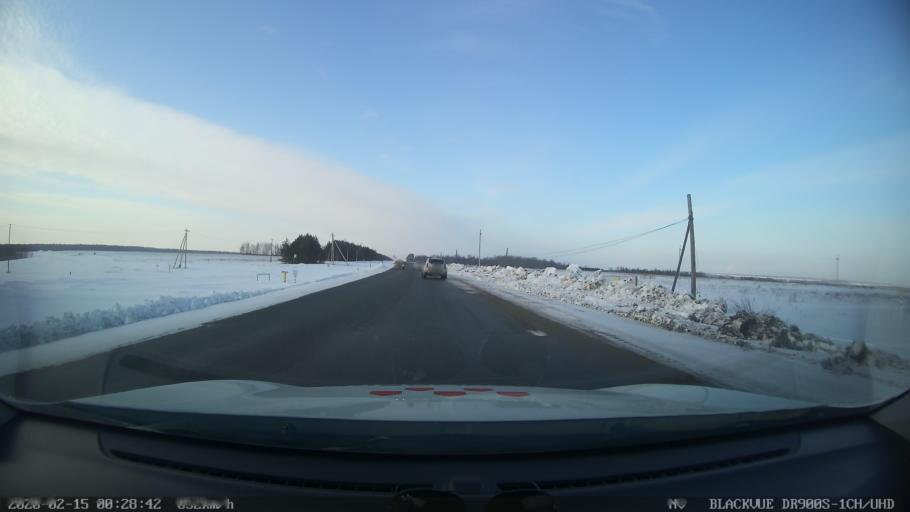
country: RU
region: Tatarstan
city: Verkhniy Uslon
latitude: 55.6444
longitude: 48.8750
